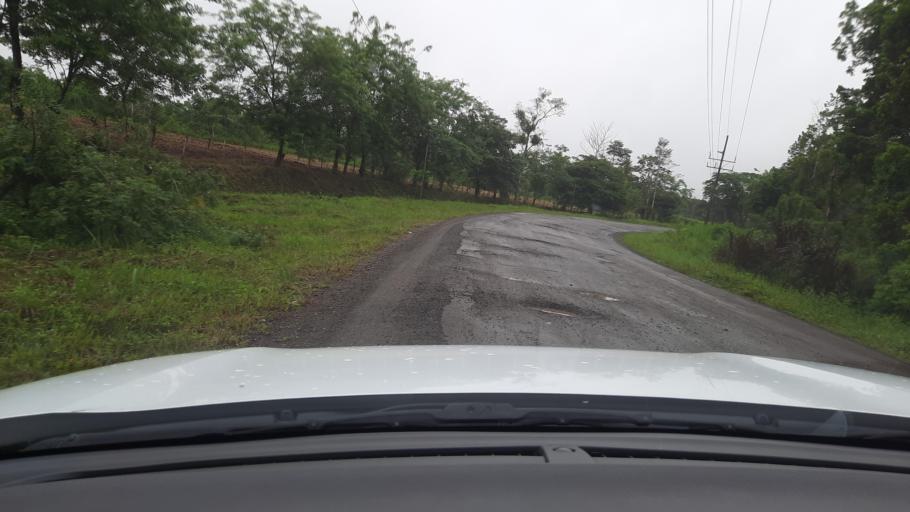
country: CR
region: Alajuela
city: San Jose
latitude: 11.0173
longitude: -85.3522
